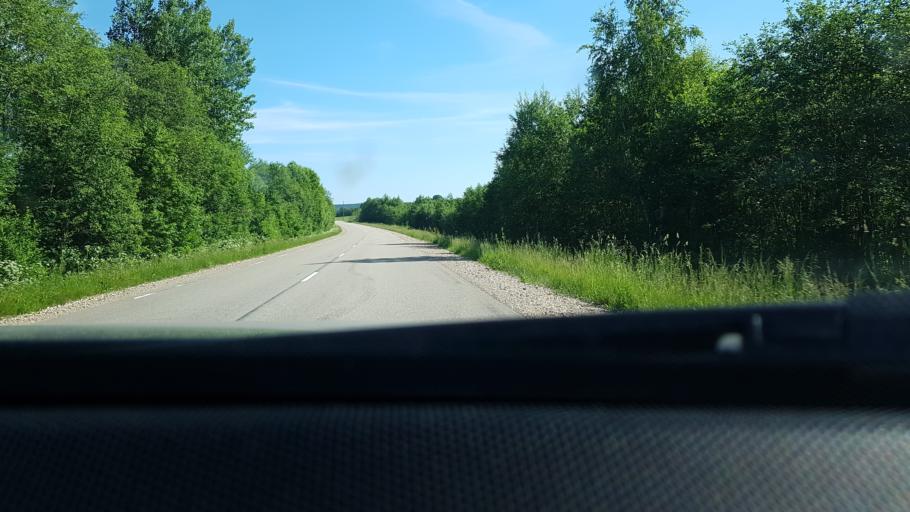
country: LV
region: Kraslavas Rajons
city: Kraslava
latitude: 55.8462
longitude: 26.9586
